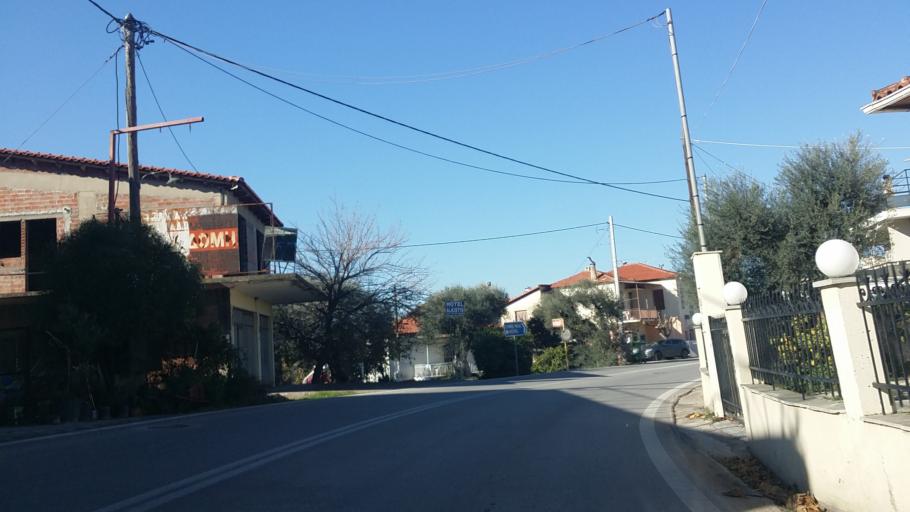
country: GR
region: West Greece
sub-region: Nomos Achaias
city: Temeni
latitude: 38.1861
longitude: 22.1965
